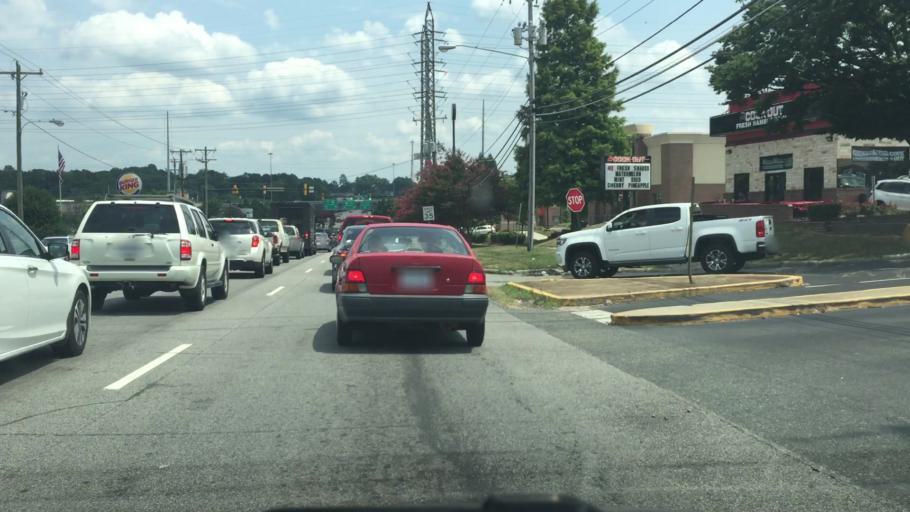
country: US
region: North Carolina
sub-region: Rowan County
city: Salisbury
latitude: 35.6609
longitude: -80.4629
